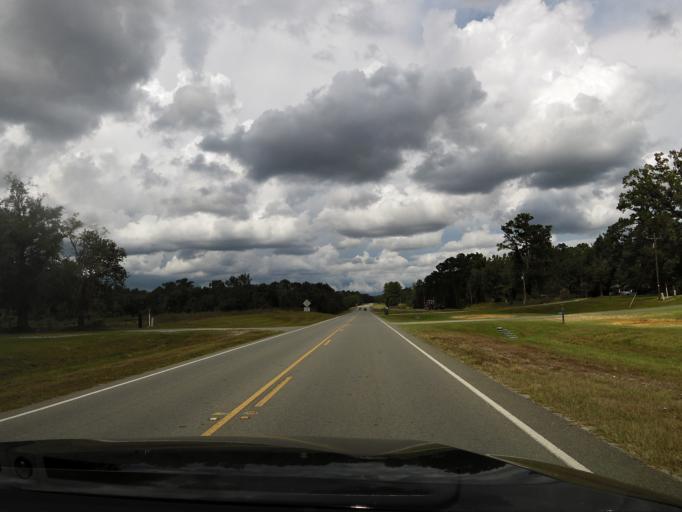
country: US
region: Georgia
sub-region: Brantley County
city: Nahunta
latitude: 31.1519
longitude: -81.9915
